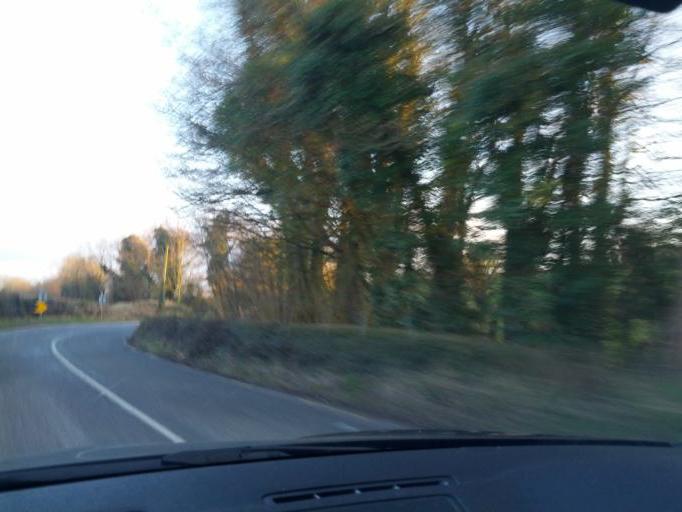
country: IE
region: Munster
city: Nenagh Bridge
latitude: 52.9541
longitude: -8.2320
